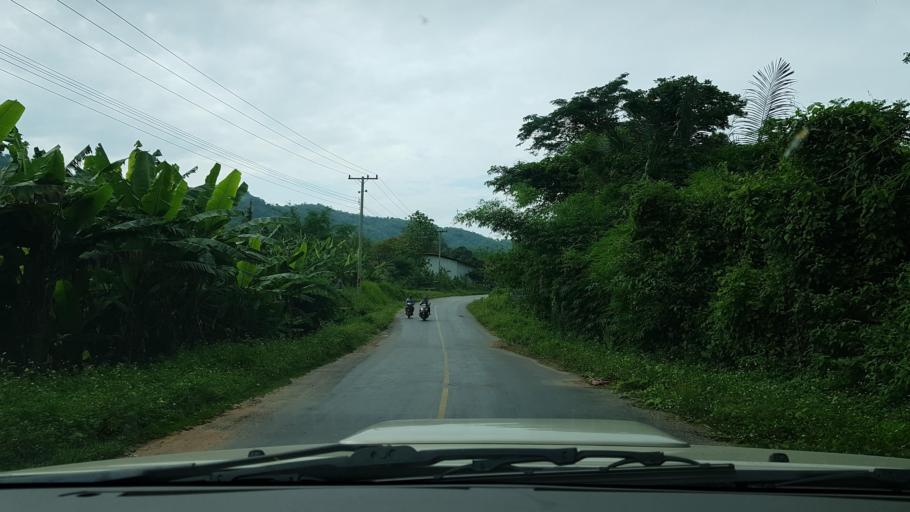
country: LA
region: Loungnamtha
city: Muang Nale
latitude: 20.3800
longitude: 101.7408
